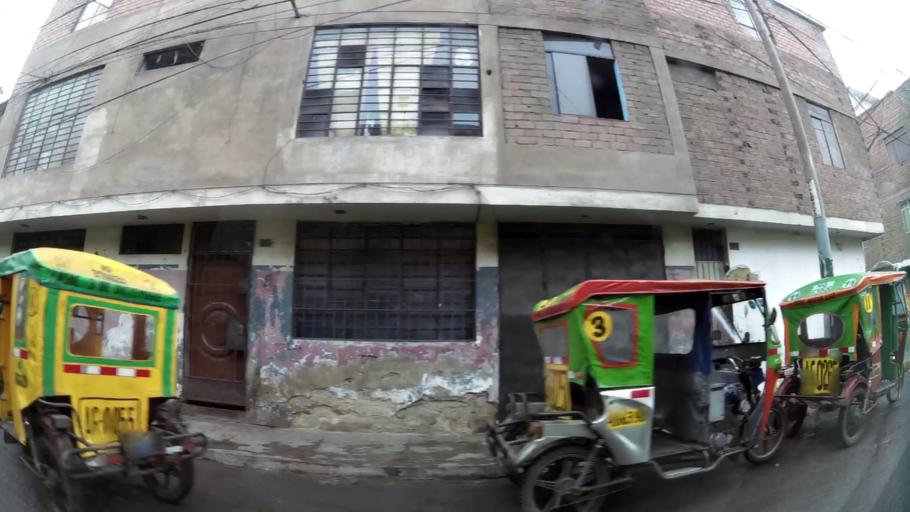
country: PE
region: Lima
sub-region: Lima
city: San Luis
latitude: -12.0536
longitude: -77.0022
